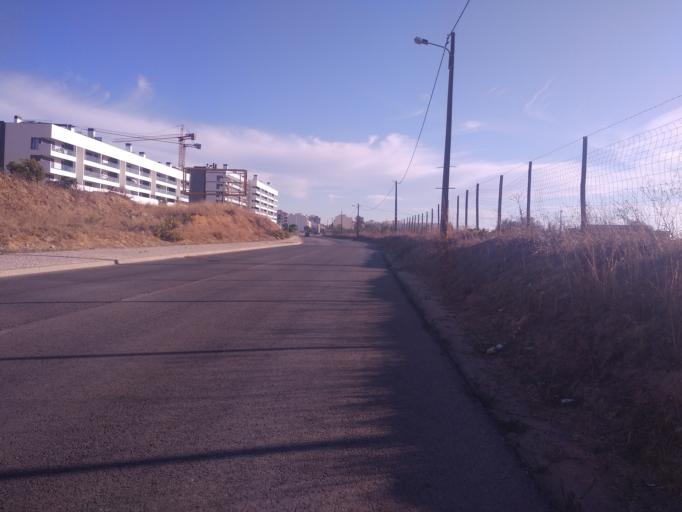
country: PT
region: Faro
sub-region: Faro
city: Faro
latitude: 37.0325
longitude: -7.9399
